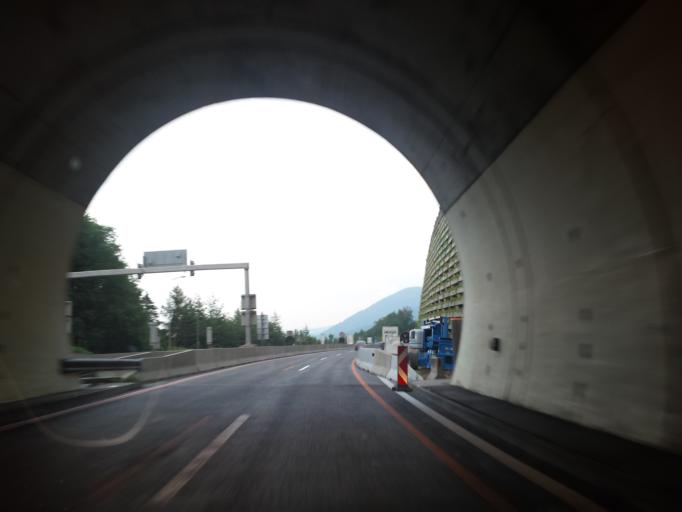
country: AT
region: Lower Austria
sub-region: Politischer Bezirk Neunkirchen
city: Schottwien
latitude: 47.6537
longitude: 15.8764
